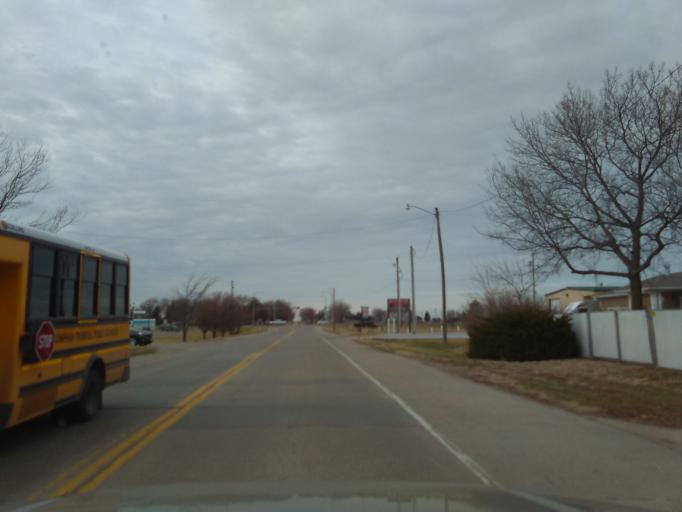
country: US
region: Nebraska
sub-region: Hall County
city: Grand Island
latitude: 40.7711
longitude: -98.3754
